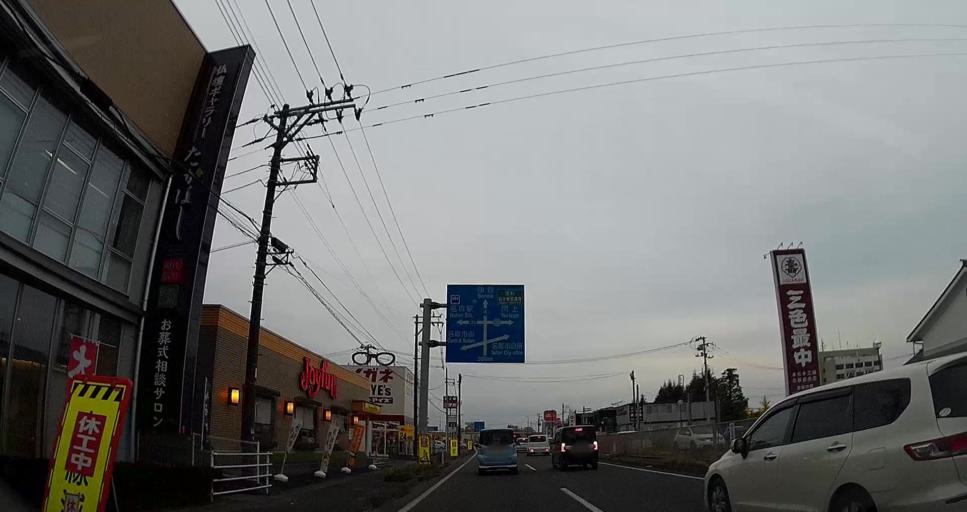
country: JP
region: Miyagi
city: Iwanuma
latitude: 38.1699
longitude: 140.8900
